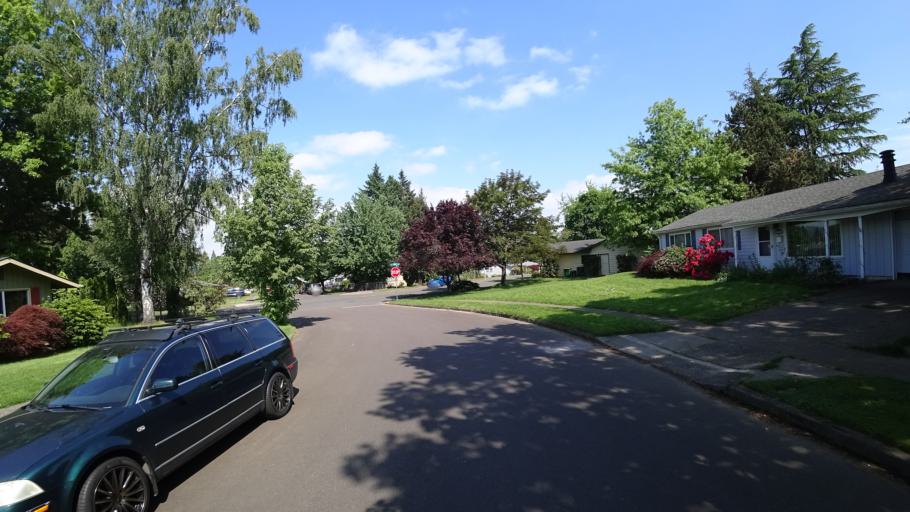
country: US
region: Oregon
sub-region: Washington County
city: Beaverton
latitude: 45.4702
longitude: -122.7947
